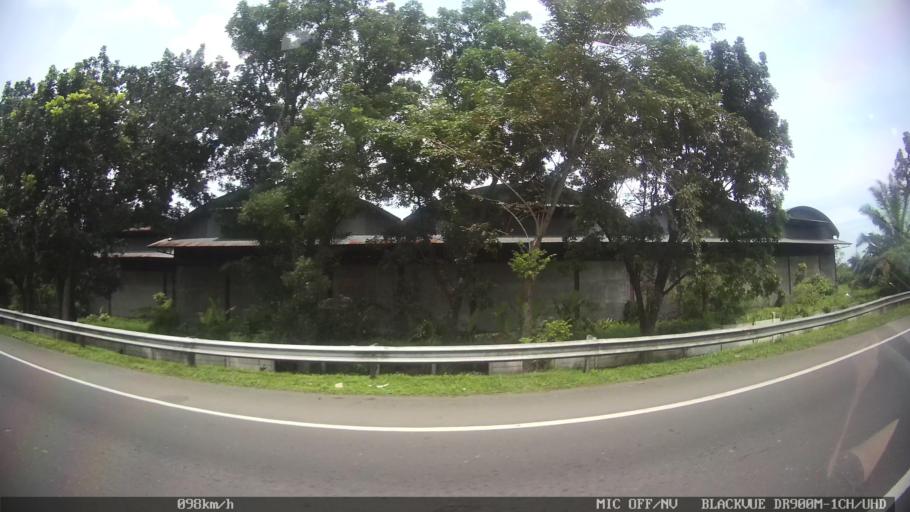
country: ID
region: North Sumatra
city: Labuhan Deli
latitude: 3.6787
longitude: 98.6803
